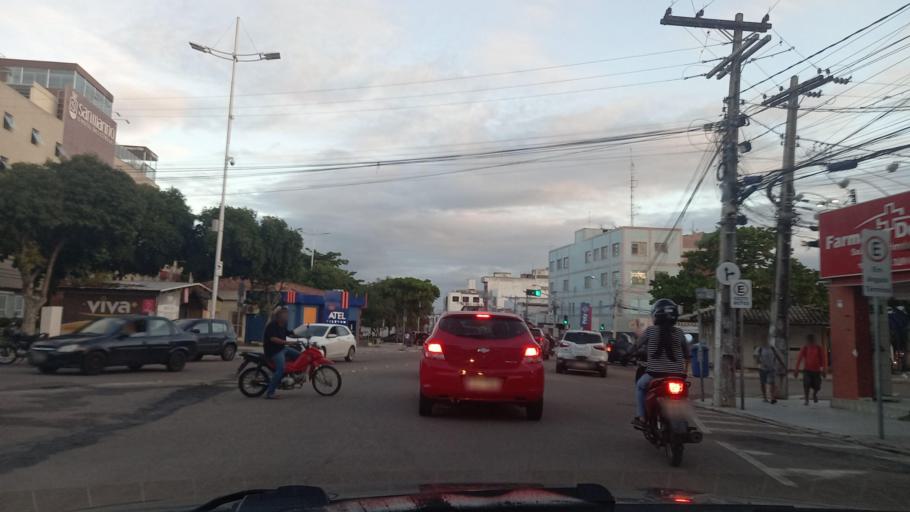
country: BR
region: Bahia
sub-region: Paulo Afonso
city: Paulo Afonso
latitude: -9.3999
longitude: -38.2176
